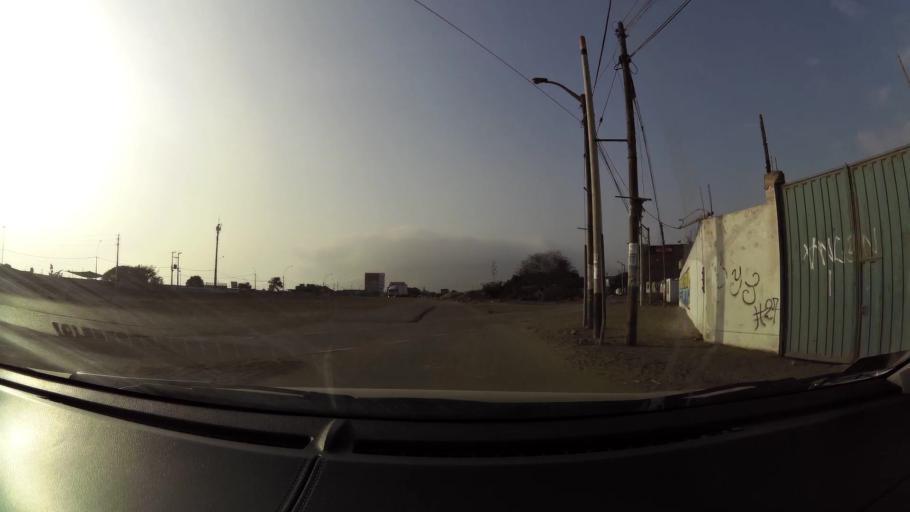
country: PE
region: Lima
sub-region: Lima
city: Santa Rosa
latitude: -11.7736
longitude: -77.1604
